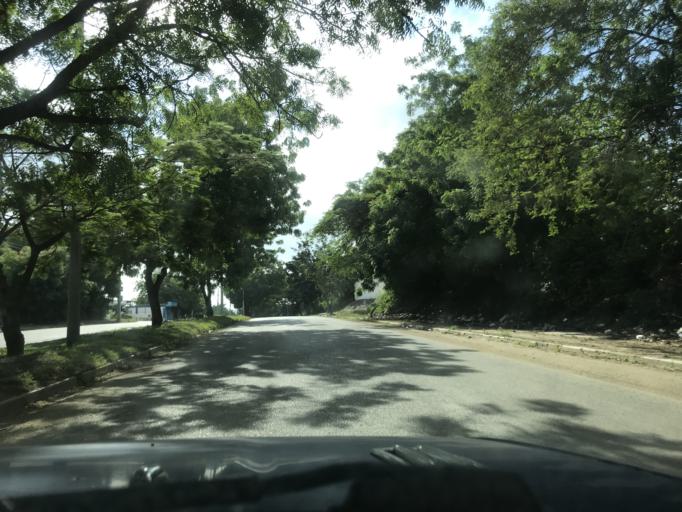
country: DO
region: Santiago
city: Santiago de los Caballeros
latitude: 19.4137
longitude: -70.7257
